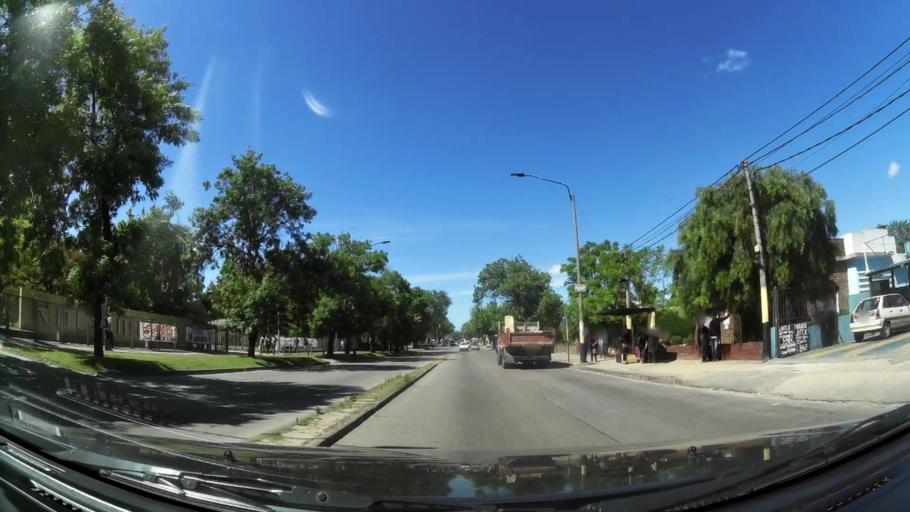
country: UY
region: Canelones
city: Paso de Carrasco
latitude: -34.8431
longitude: -56.1250
